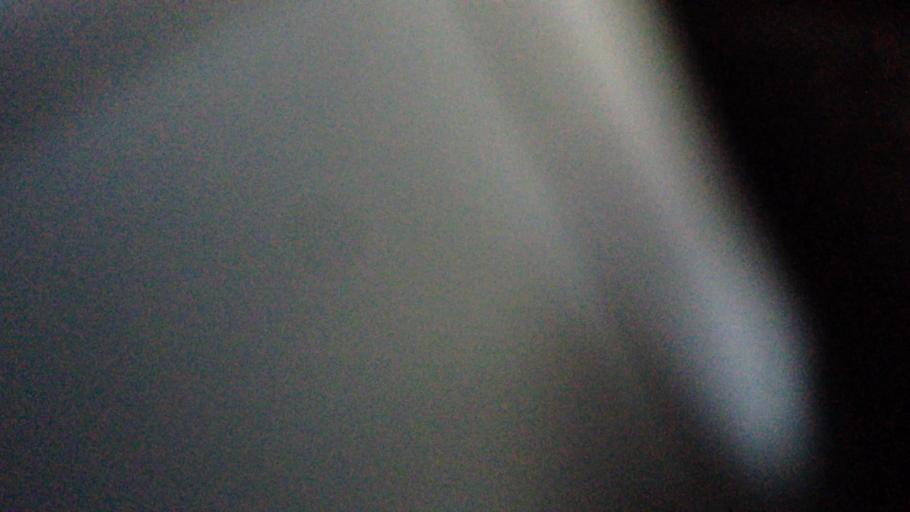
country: US
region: New York
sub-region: Columbia County
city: Hudson
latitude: 42.2540
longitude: -73.7891
